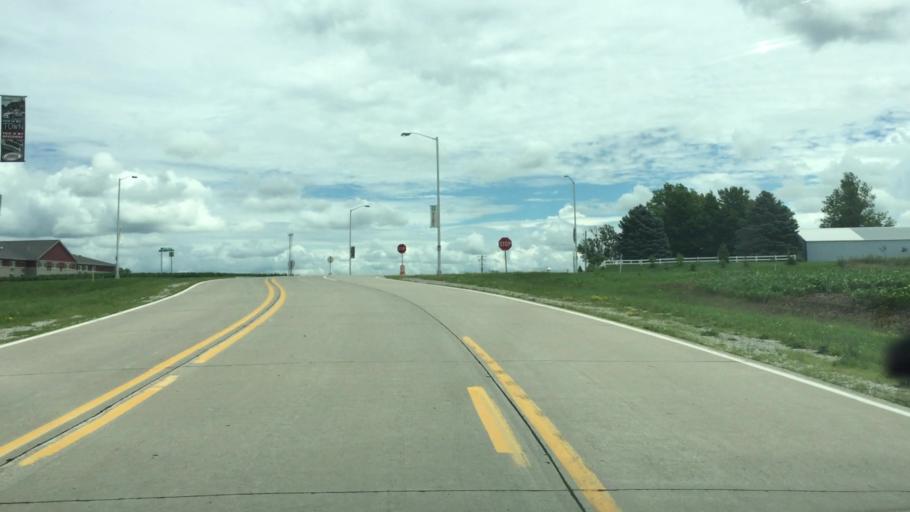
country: US
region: Iowa
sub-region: Jasper County
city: Newton
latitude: 41.6777
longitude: -93.0013
